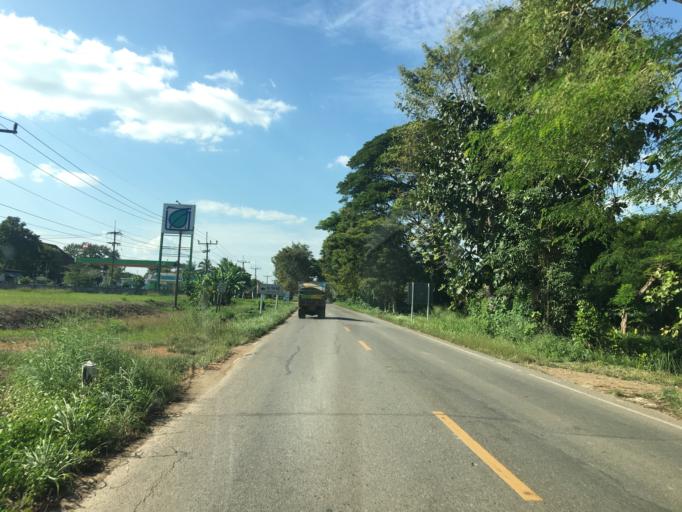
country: TH
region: Phayao
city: Chun
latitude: 19.3300
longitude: 100.1413
